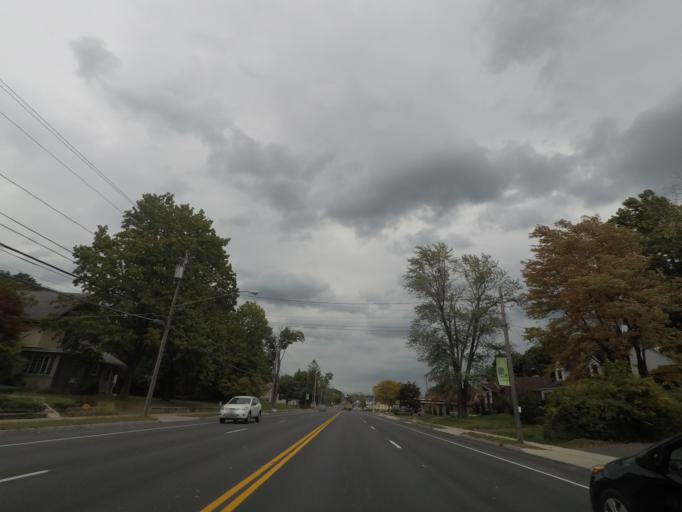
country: US
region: New York
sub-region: Albany County
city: McKownville
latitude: 42.6793
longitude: -73.8321
